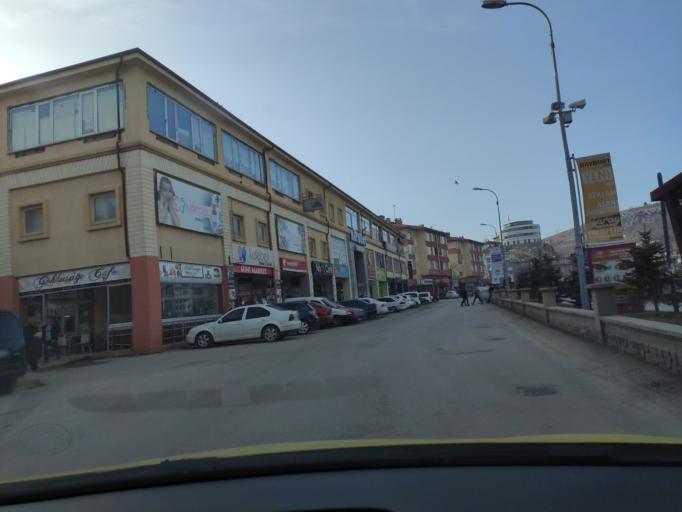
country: TR
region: Bayburt
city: Bayburt
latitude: 40.2523
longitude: 40.2284
